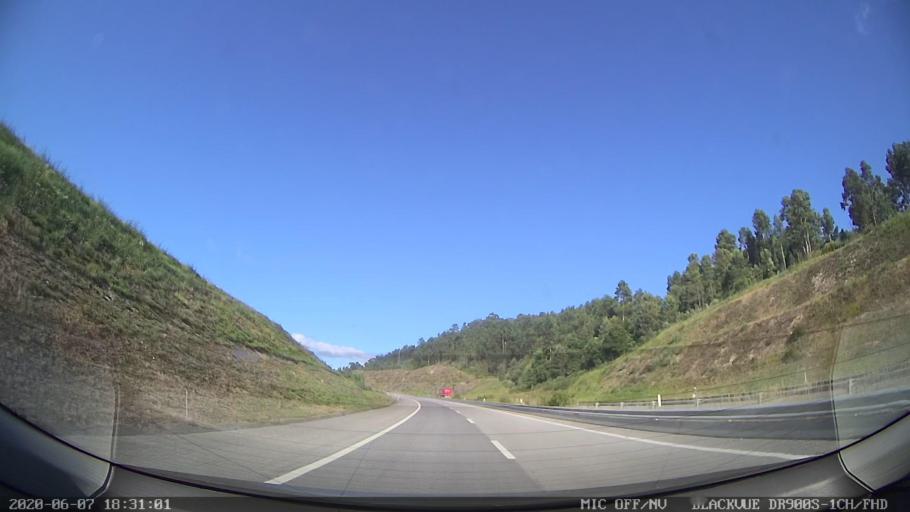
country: PT
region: Braga
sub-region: Fafe
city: Fafe
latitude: 41.4341
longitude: -8.1381
